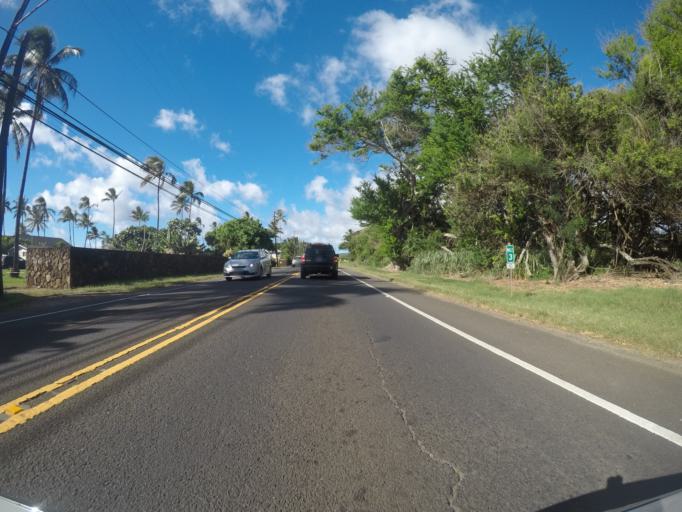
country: US
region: Hawaii
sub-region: Honolulu County
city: Hale'iwa
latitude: 21.6143
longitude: -158.0896
